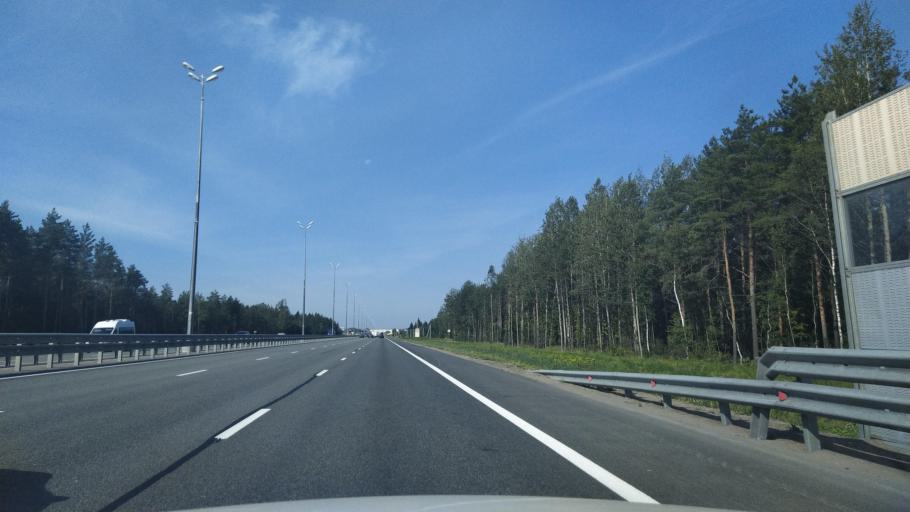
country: RU
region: Leningrad
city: Gatchina
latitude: 59.5260
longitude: 30.1093
